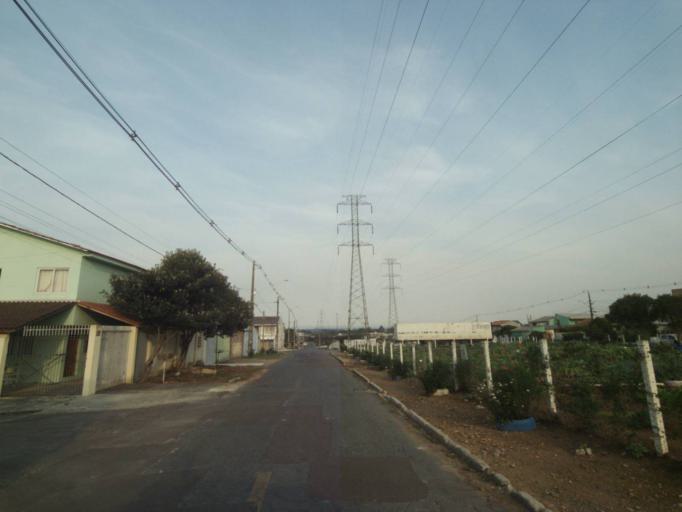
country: BR
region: Parana
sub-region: Pinhais
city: Pinhais
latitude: -25.4825
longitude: -49.2046
